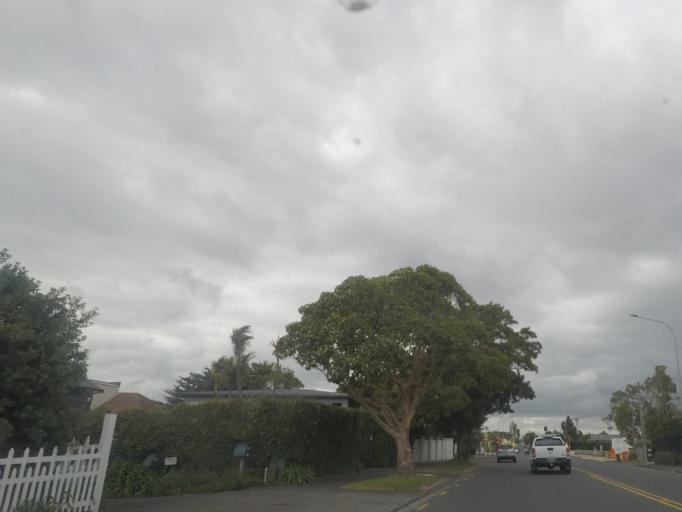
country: NZ
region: Auckland
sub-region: Auckland
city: Tamaki
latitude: -36.8673
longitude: 174.8452
